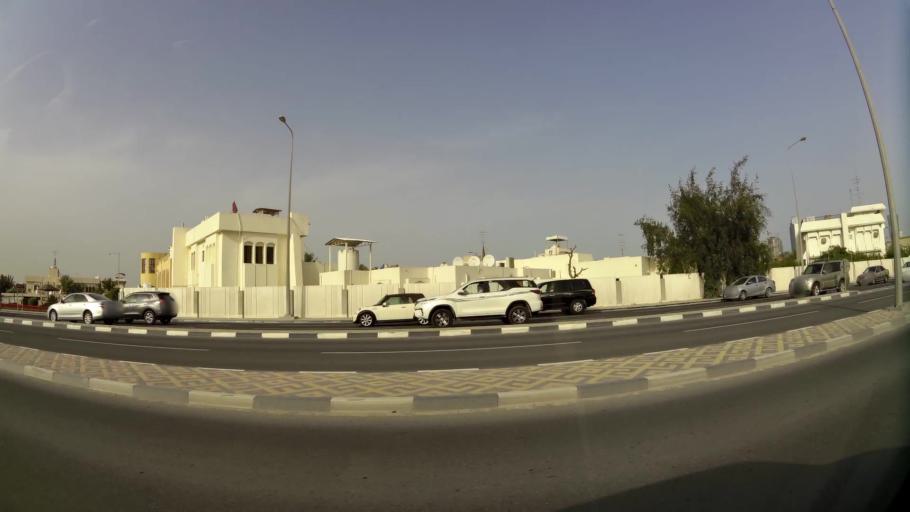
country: QA
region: Baladiyat ad Dawhah
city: Doha
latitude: 25.3270
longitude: 51.5070
